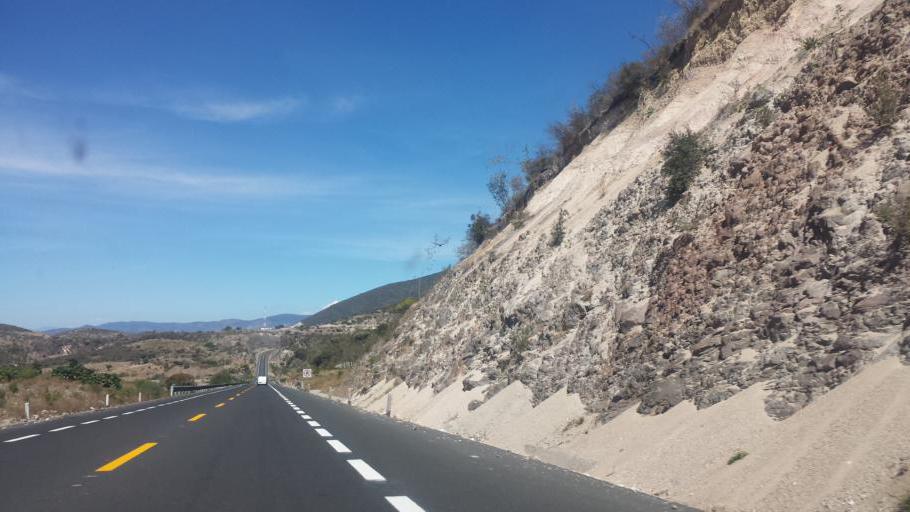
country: MX
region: Oaxaca
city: San Gabriel Casa Blanca
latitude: 17.9654
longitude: -97.3575
